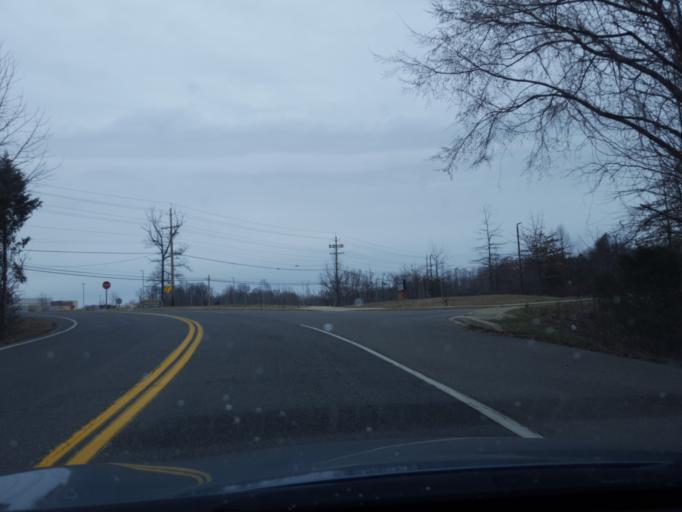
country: US
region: Maryland
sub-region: Calvert County
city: Prince Frederick
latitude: 38.5503
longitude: -76.5824
